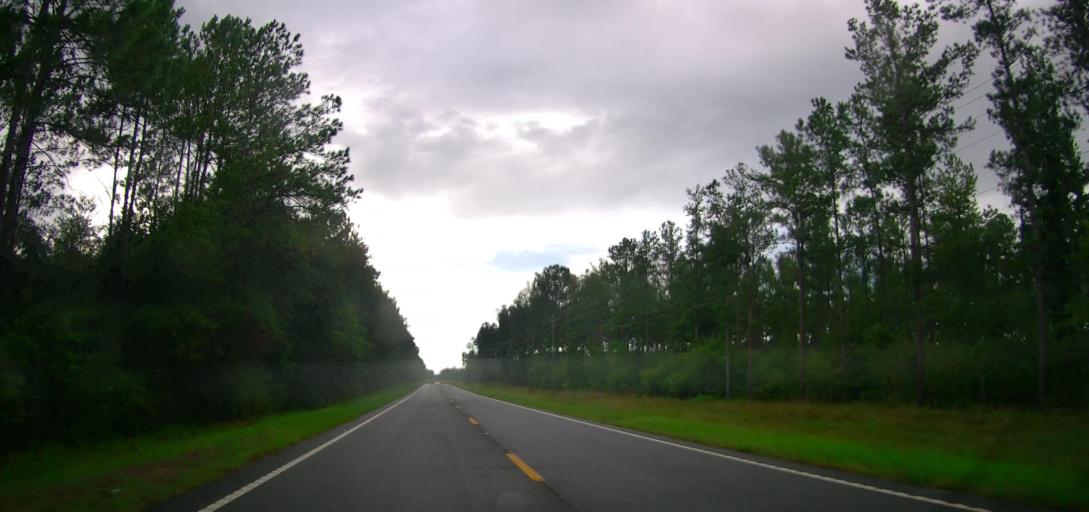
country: US
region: Georgia
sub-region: Ware County
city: Deenwood
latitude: 31.2759
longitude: -82.5331
